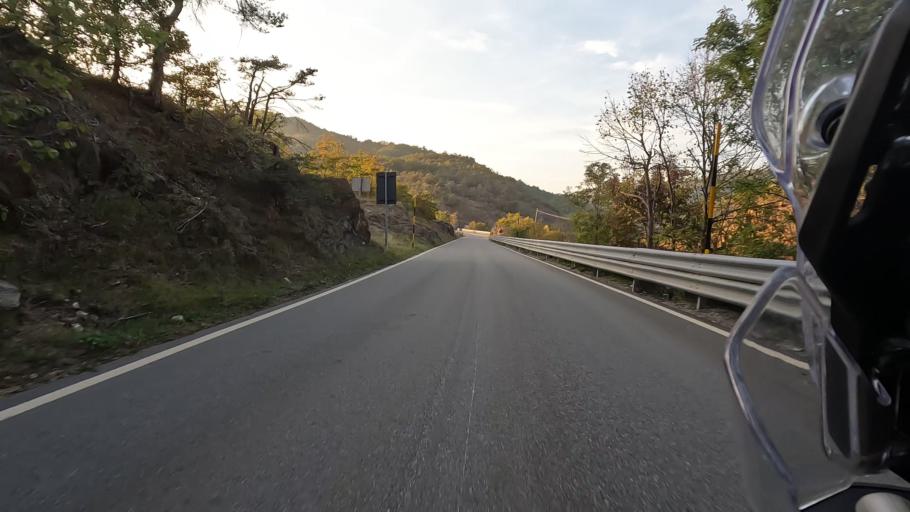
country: IT
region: Liguria
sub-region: Provincia di Savona
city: Sassello
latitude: 44.5204
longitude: 8.4712
